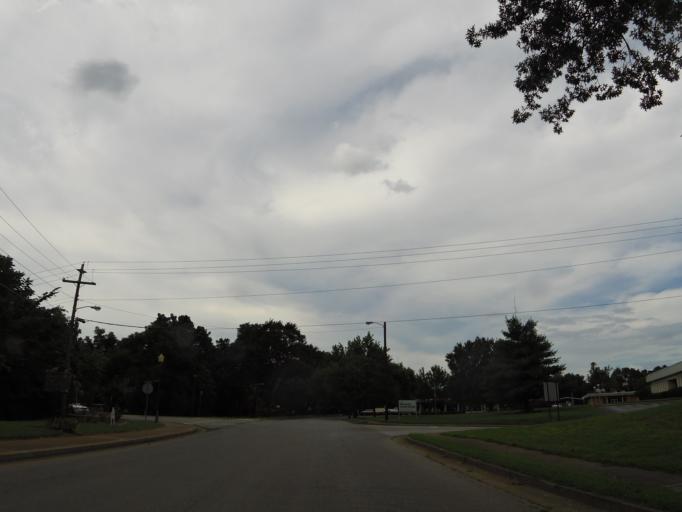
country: US
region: Kentucky
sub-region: Christian County
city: Hopkinsville
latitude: 36.8695
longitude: -87.4885
